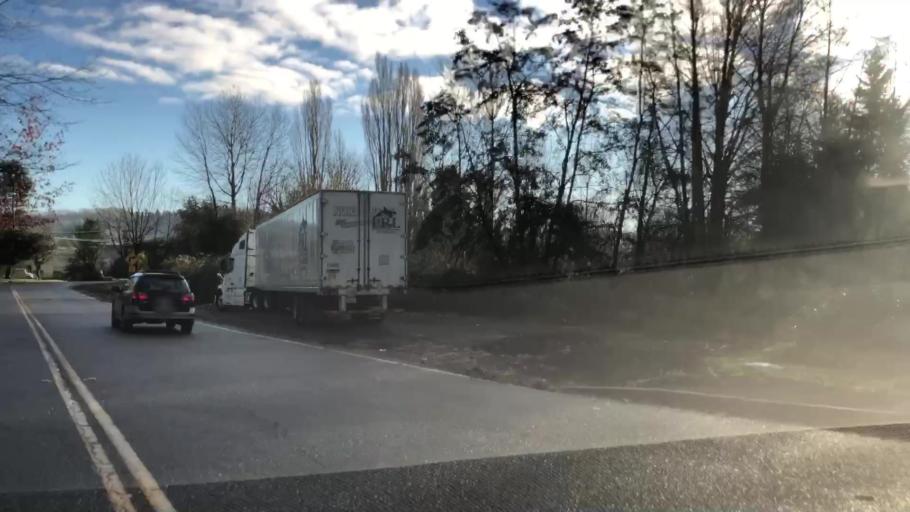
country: US
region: Washington
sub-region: King County
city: Tukwila
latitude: 47.4400
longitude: -122.2327
